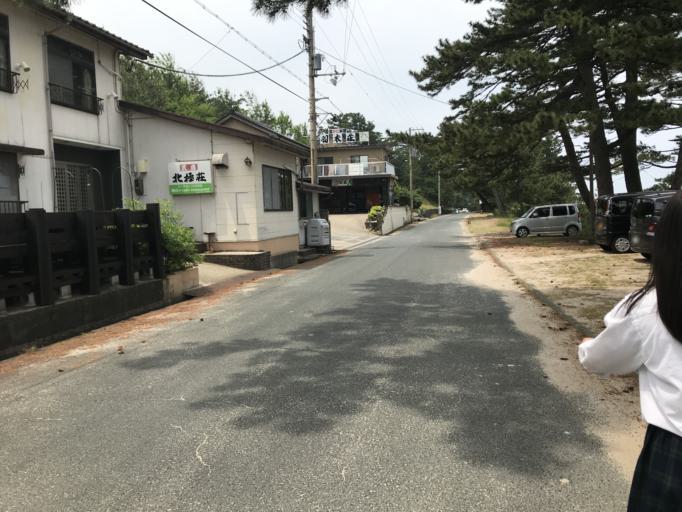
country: JP
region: Kyoto
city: Miyazu
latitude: 35.7020
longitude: 135.0486
